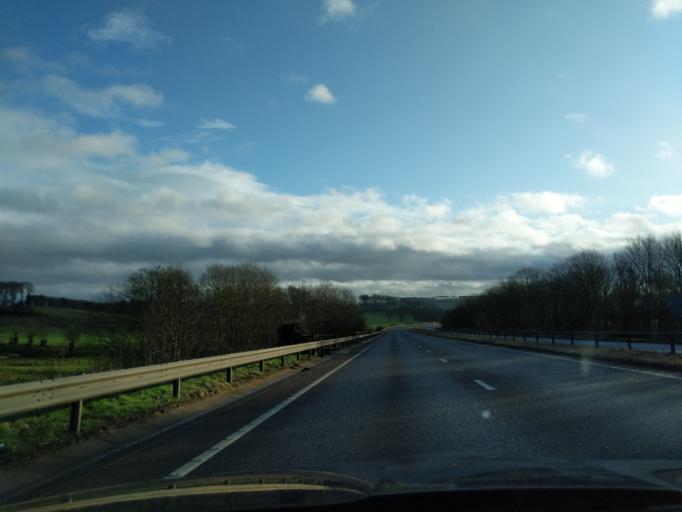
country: GB
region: England
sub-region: Northumberland
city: Alnwick
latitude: 55.4192
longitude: -1.6802
